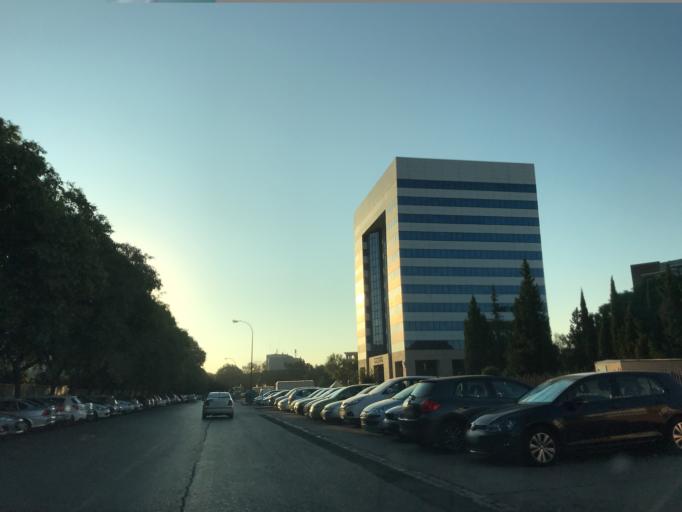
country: ES
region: Andalusia
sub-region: Provincia de Sevilla
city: Sevilla
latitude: 37.4070
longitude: -5.9317
